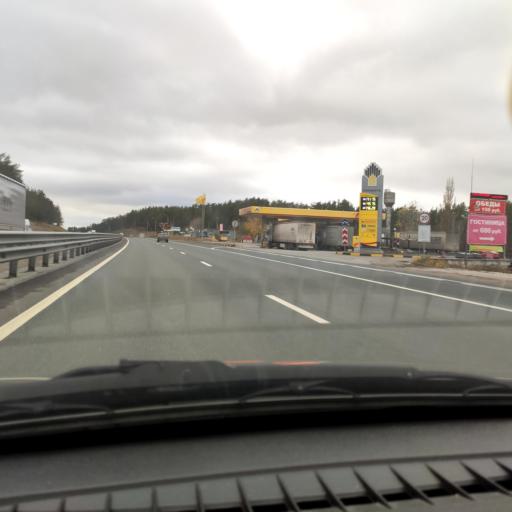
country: RU
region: Samara
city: Zhigulevsk
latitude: 53.5112
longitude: 49.5665
